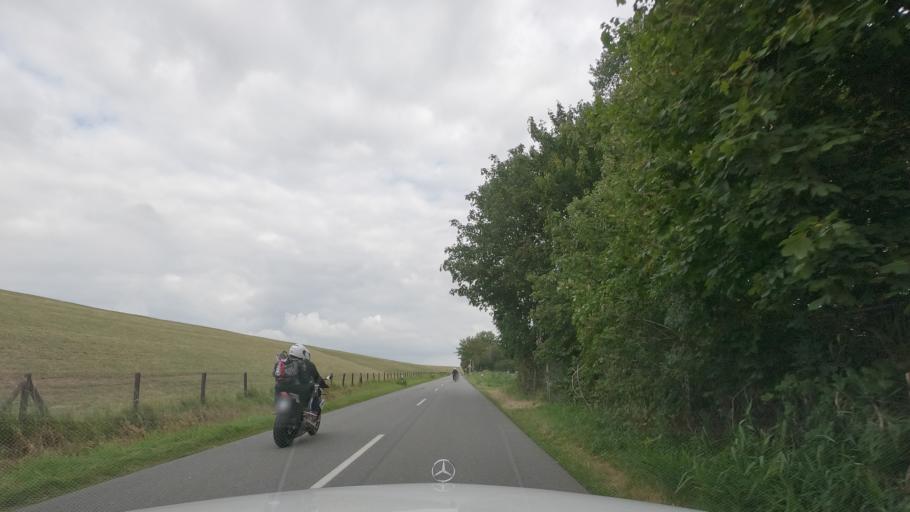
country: DE
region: Lower Saxony
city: Brake (Unterweser)
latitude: 53.3017
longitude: 8.5280
